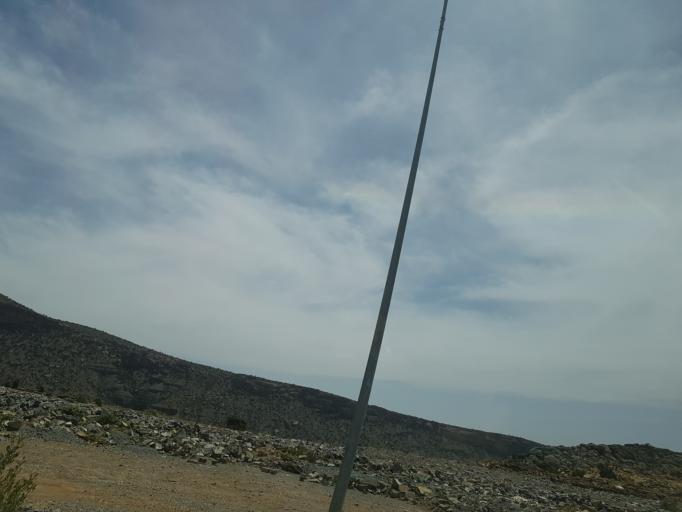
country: OM
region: Al Batinah
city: Bayt al `Awabi
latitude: 23.1373
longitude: 57.5468
